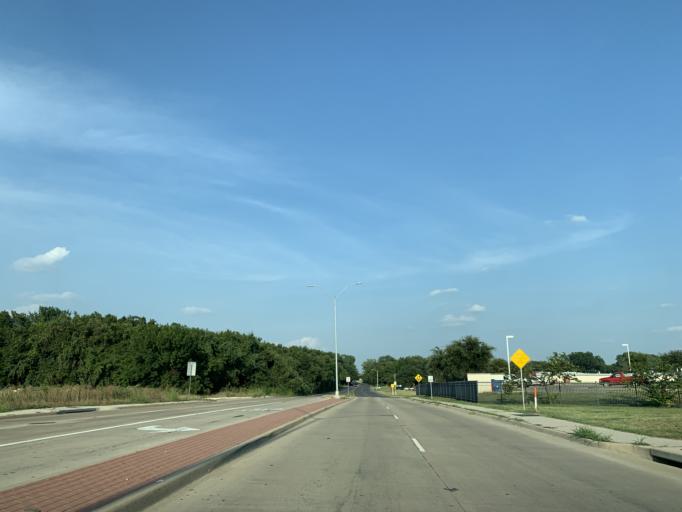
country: US
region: Texas
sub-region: Tarrant County
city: Hurst
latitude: 32.8023
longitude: -97.1830
